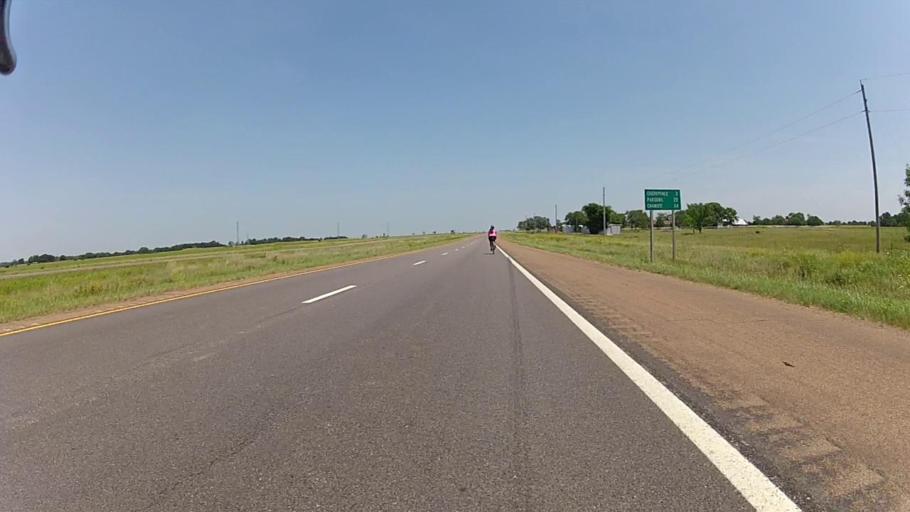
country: US
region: Kansas
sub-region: Montgomery County
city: Cherryvale
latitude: 37.2248
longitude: -95.5855
